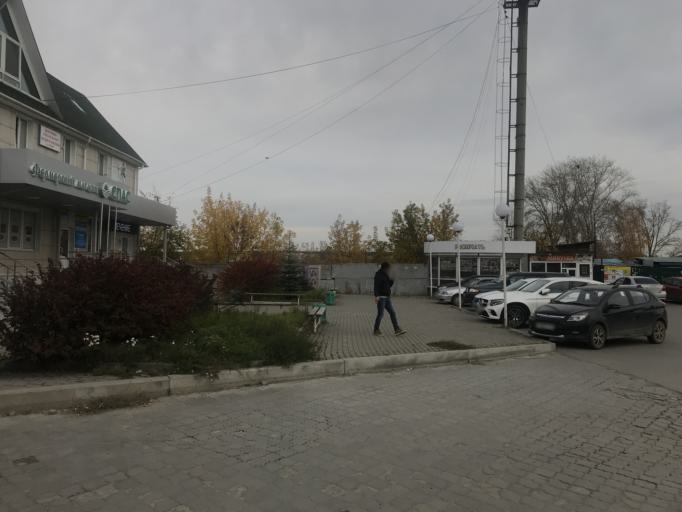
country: RU
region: Sverdlovsk
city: Aramil
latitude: 56.7008
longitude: 60.8289
